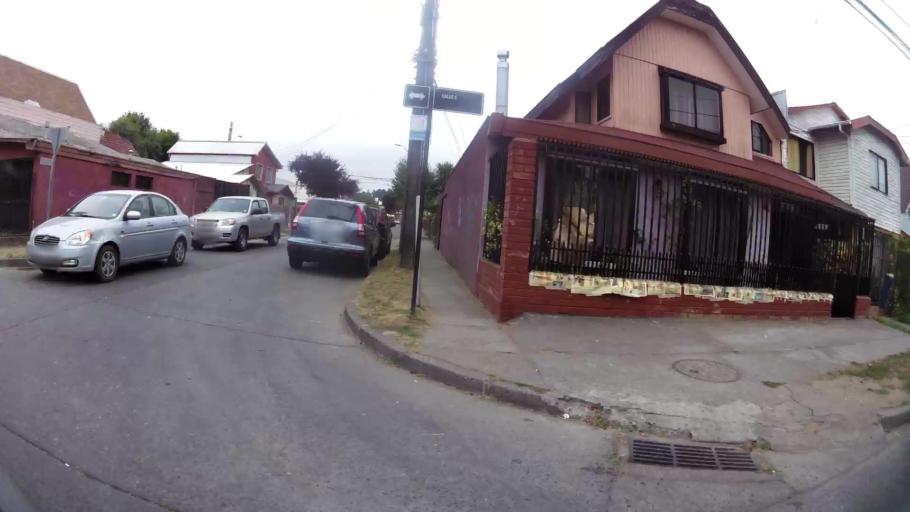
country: CL
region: Biobio
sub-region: Provincia de Concepcion
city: Concepcion
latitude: -36.8288
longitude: -73.0109
